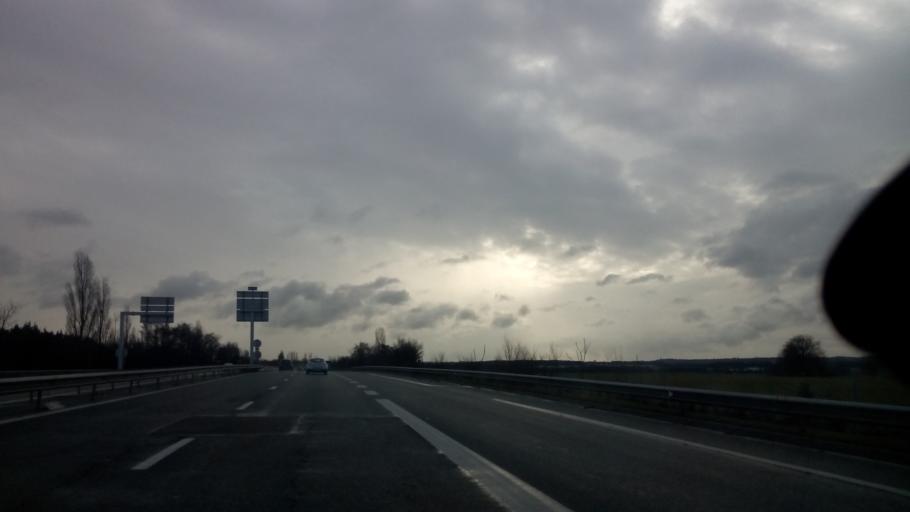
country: FR
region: Rhone-Alpes
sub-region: Departement du Rhone
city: Corbas
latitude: 45.6693
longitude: 4.9152
